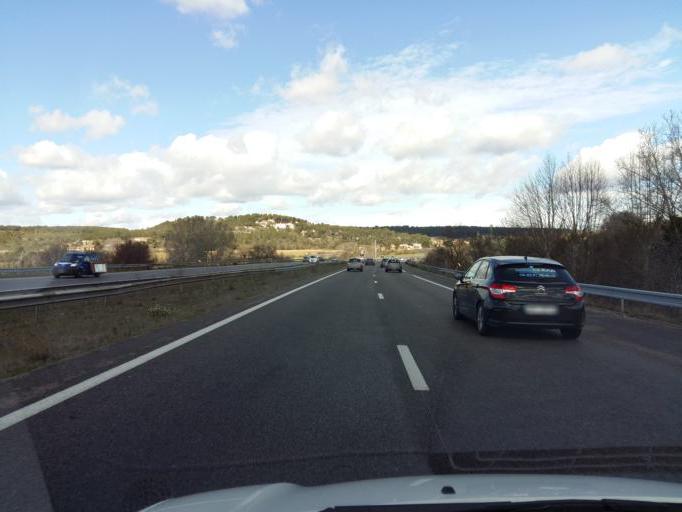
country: FR
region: Provence-Alpes-Cote d'Azur
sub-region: Departement des Bouches-du-Rhone
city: Bouc-Bel-Air
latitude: 43.4483
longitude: 5.3960
